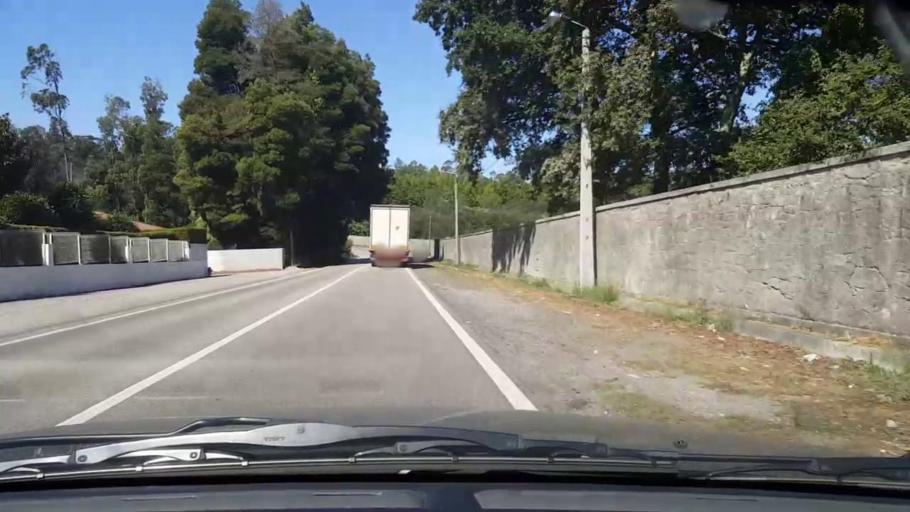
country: PT
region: Porto
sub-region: Vila do Conde
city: Arvore
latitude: 41.3387
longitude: -8.6913
